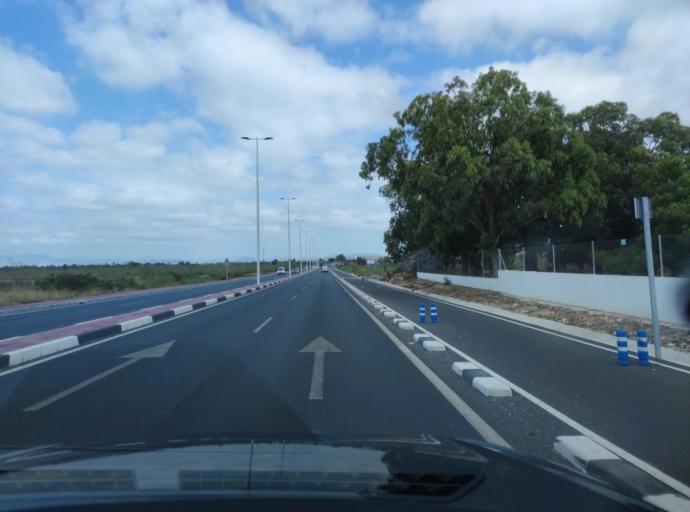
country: ES
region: Valencia
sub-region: Provincia de Alicante
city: Santa Pola
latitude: 38.2130
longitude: -0.5907
